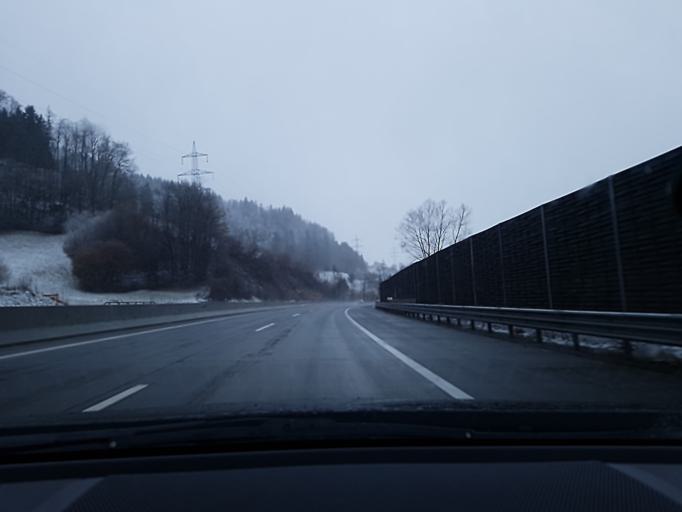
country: AT
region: Salzburg
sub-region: Politischer Bezirk Hallein
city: Kuchl
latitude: 47.6142
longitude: 13.1397
